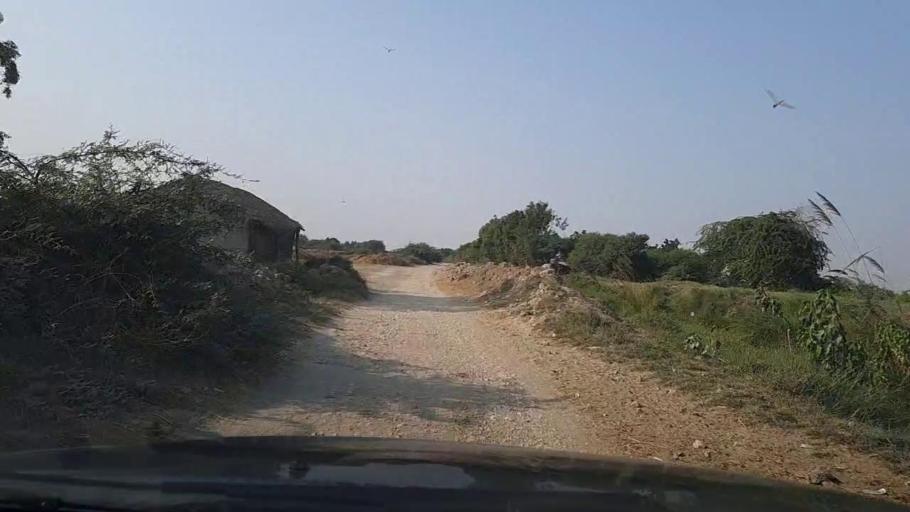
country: PK
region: Sindh
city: Mirpur Sakro
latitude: 24.6364
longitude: 67.7516
